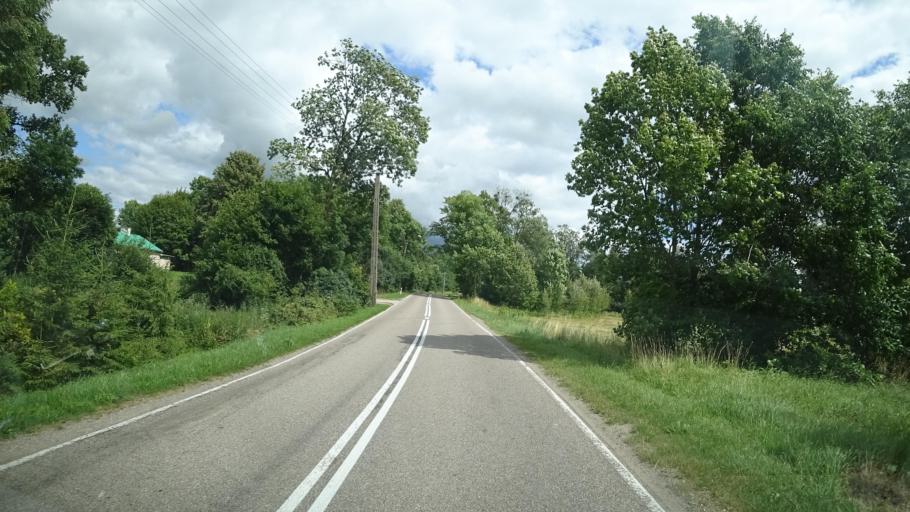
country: PL
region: Warmian-Masurian Voivodeship
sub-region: Powiat goldapski
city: Goldap
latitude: 54.2087
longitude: 22.1868
